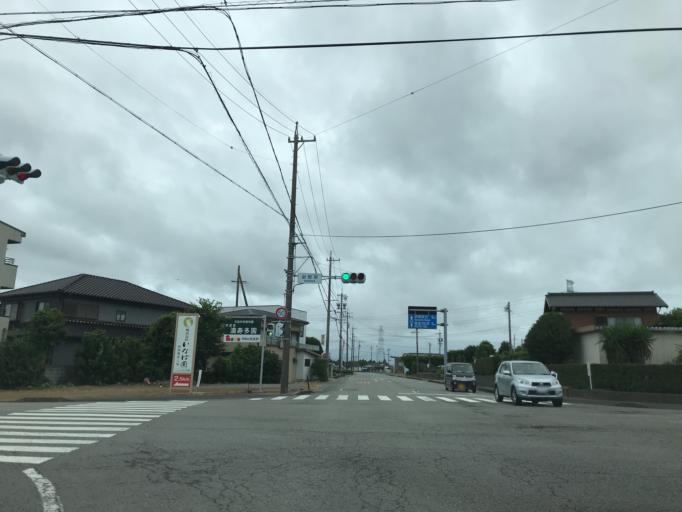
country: JP
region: Shizuoka
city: Sagara
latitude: 34.6982
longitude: 138.1447
